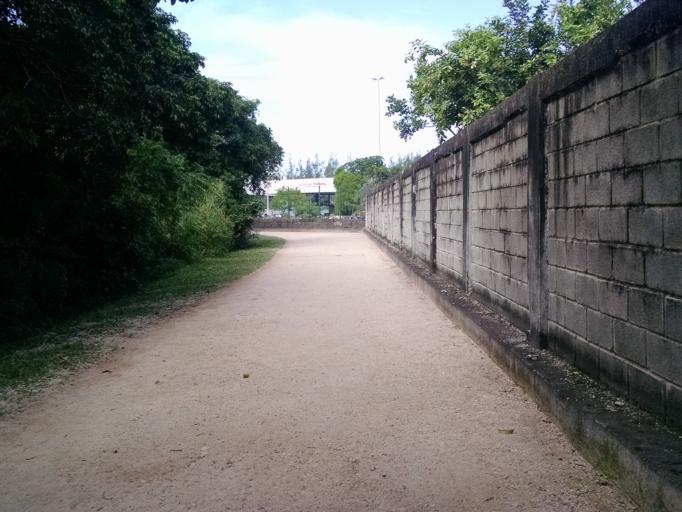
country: BR
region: Rio de Janeiro
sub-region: Rio De Janeiro
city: Rio de Janeiro
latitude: -22.9995
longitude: -43.3740
